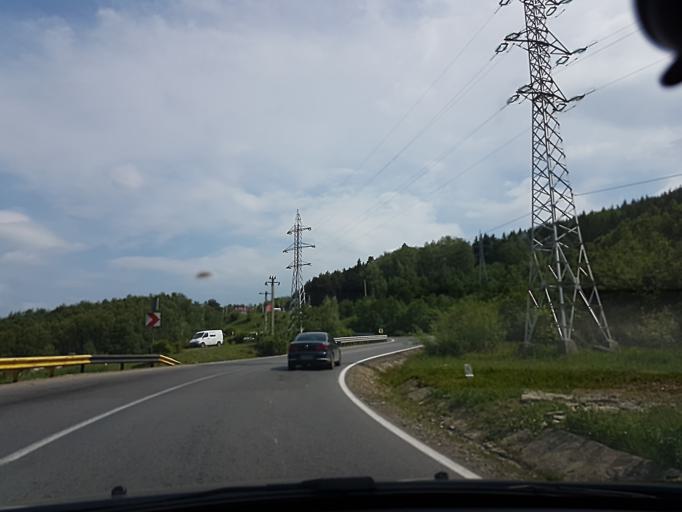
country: RO
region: Prahova
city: Maneciu
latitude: 45.3347
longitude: 25.9670
